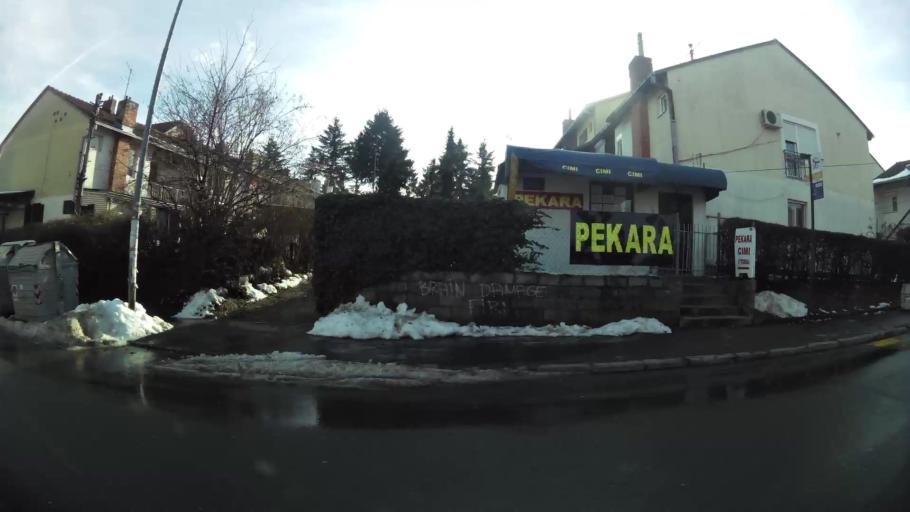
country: RS
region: Central Serbia
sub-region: Belgrade
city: Rakovica
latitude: 44.7201
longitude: 20.4255
